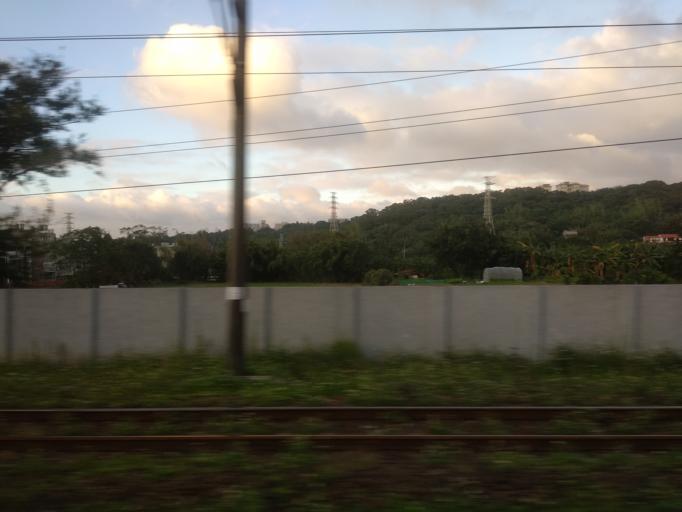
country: TW
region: Taiwan
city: Daxi
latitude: 24.9143
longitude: 121.1484
